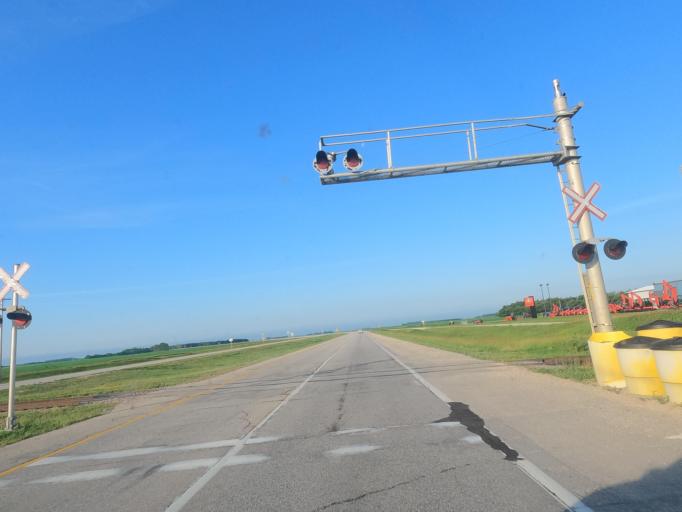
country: CA
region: Manitoba
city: Headingley
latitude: 49.9819
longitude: -97.3162
